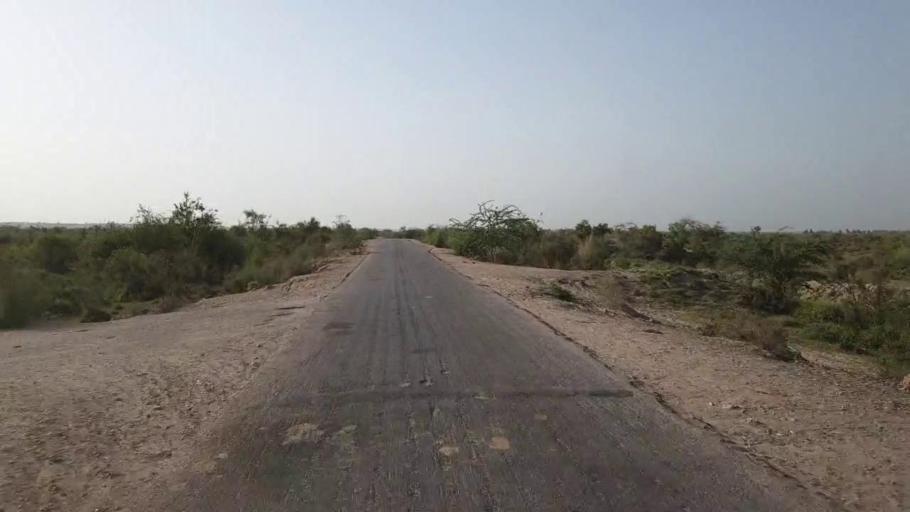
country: PK
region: Sindh
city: Jam Sahib
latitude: 26.4527
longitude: 68.8618
